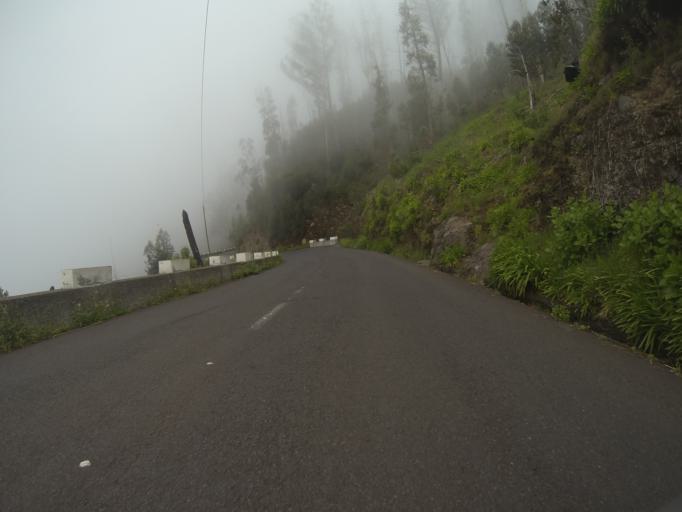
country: PT
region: Madeira
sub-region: Funchal
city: Nossa Senhora do Monte
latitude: 32.6887
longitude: -16.9012
